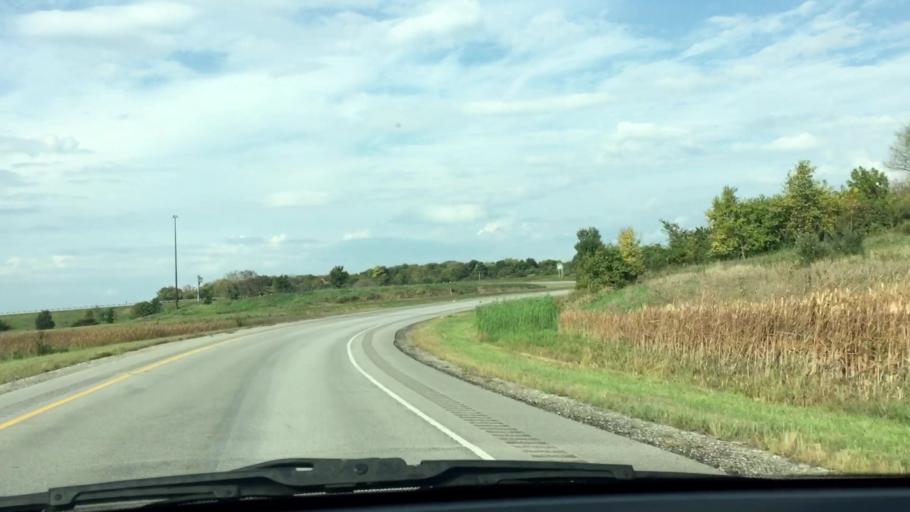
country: US
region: Illinois
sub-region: Henry County
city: Colona
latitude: 41.5375
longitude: -90.3371
